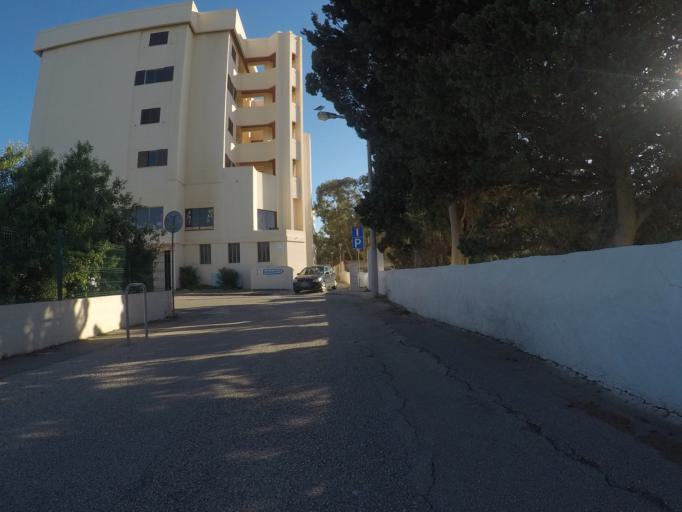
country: PT
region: Faro
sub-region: Lagos
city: Lagos
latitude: 37.0946
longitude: -8.6704
